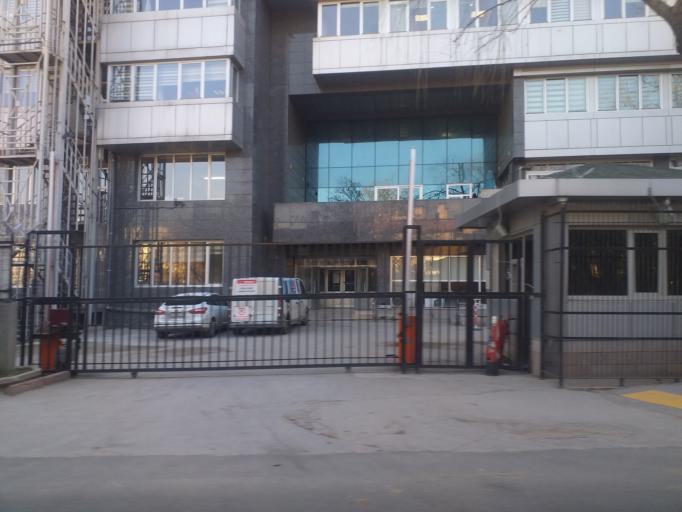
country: TR
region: Ankara
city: Ankara
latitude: 39.9397
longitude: 32.8243
